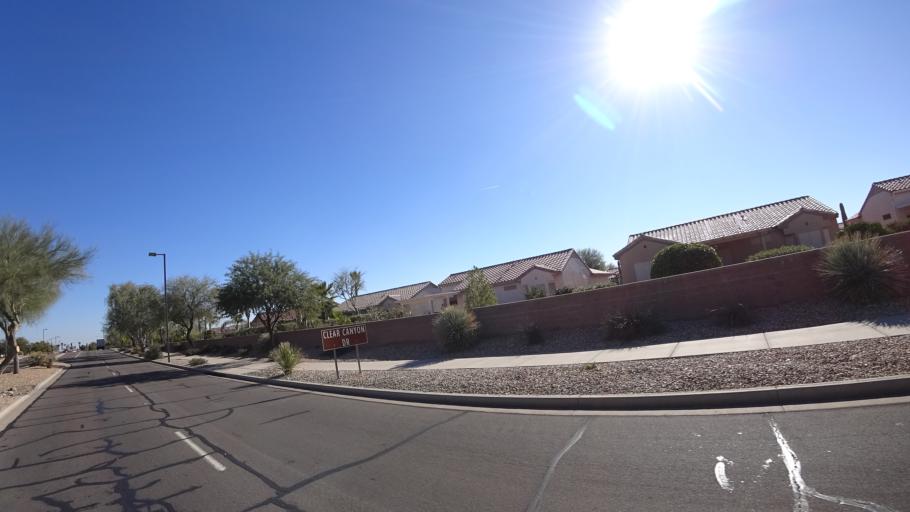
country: US
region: Arizona
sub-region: Maricopa County
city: Sun City West
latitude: 33.6676
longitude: -112.3958
